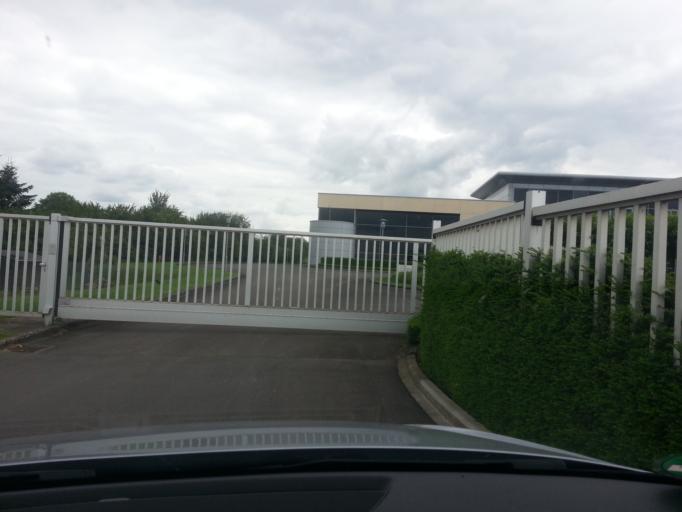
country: LU
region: Grevenmacher
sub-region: Canton de Remich
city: Mondorf-les-Bains
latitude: 49.5160
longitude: 6.3053
